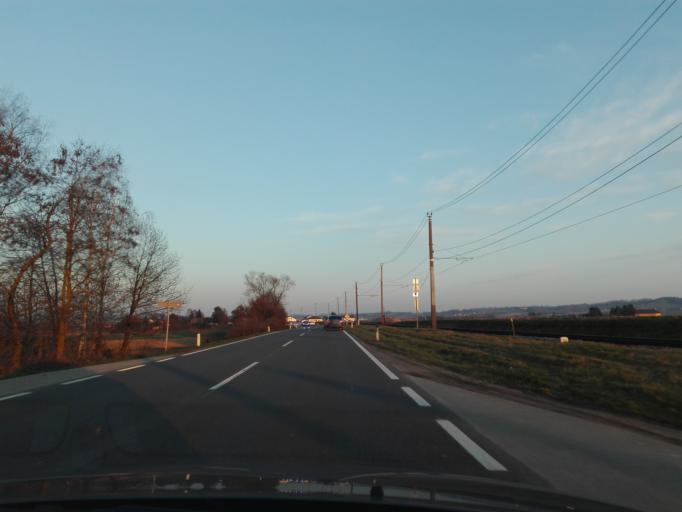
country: AT
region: Upper Austria
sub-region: Politischer Bezirk Urfahr-Umgebung
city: Goldworth
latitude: 48.2887
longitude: 14.0655
